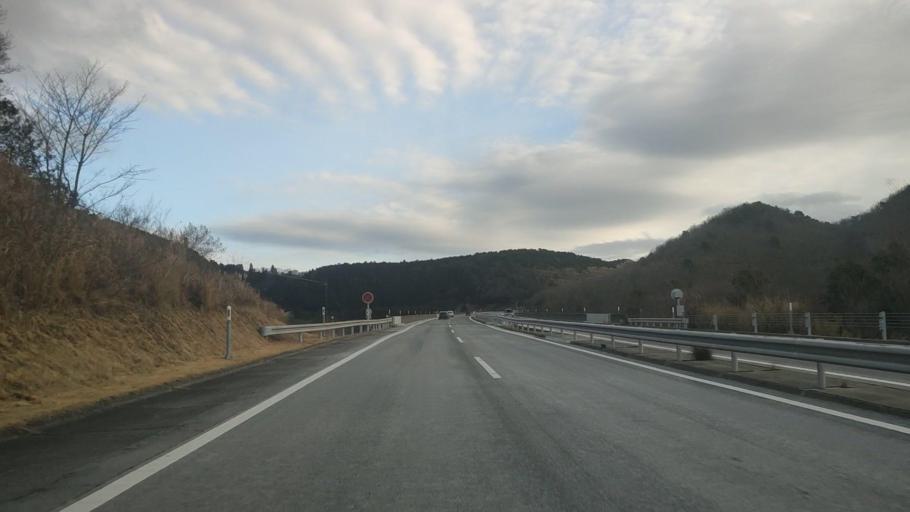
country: JP
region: Oita
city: Beppu
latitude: 33.2911
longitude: 131.3529
